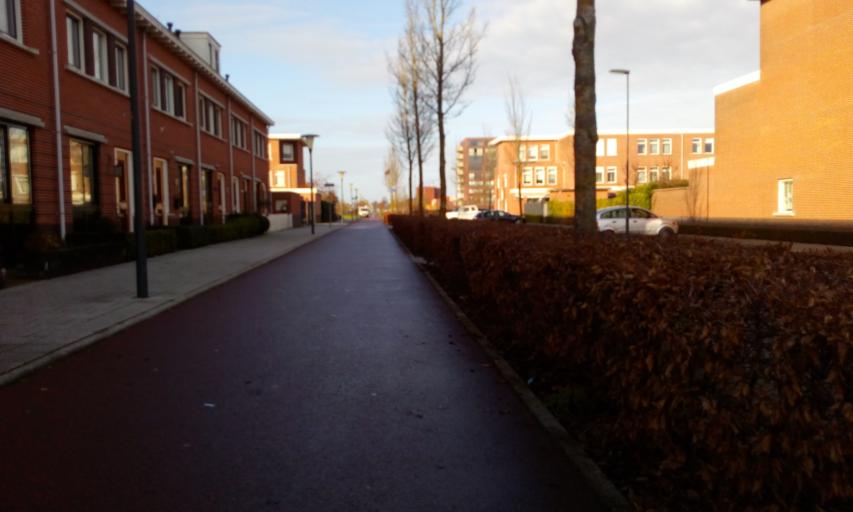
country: NL
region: South Holland
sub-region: Gemeente Rijnwoude
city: Benthuizen
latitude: 52.0568
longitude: 4.5384
